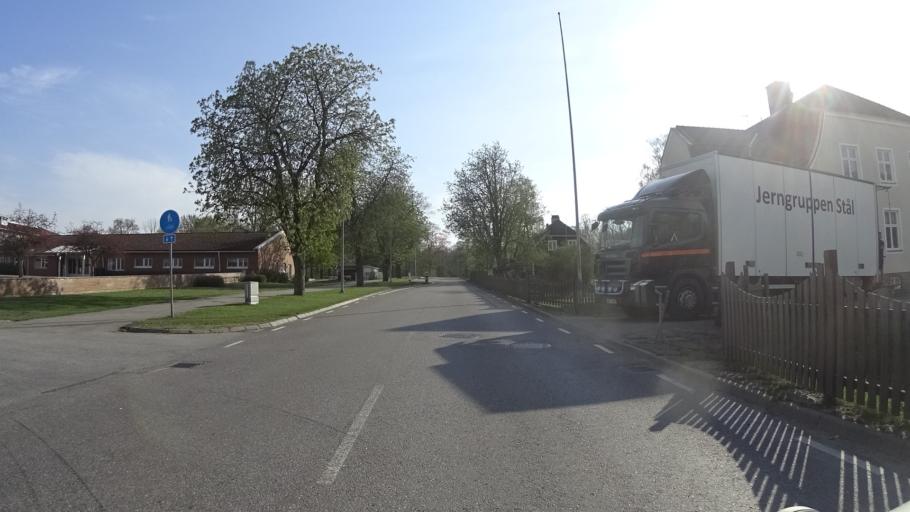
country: SE
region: Vaestra Goetaland
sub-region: Gotene Kommun
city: Goetene
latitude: 58.6289
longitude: 13.4321
